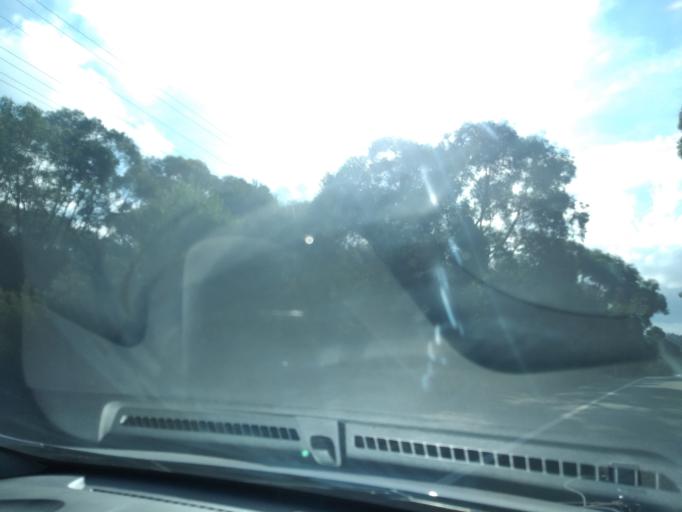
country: AU
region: New South Wales
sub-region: Wollongong
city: Helensburgh
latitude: -34.2175
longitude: 150.9783
